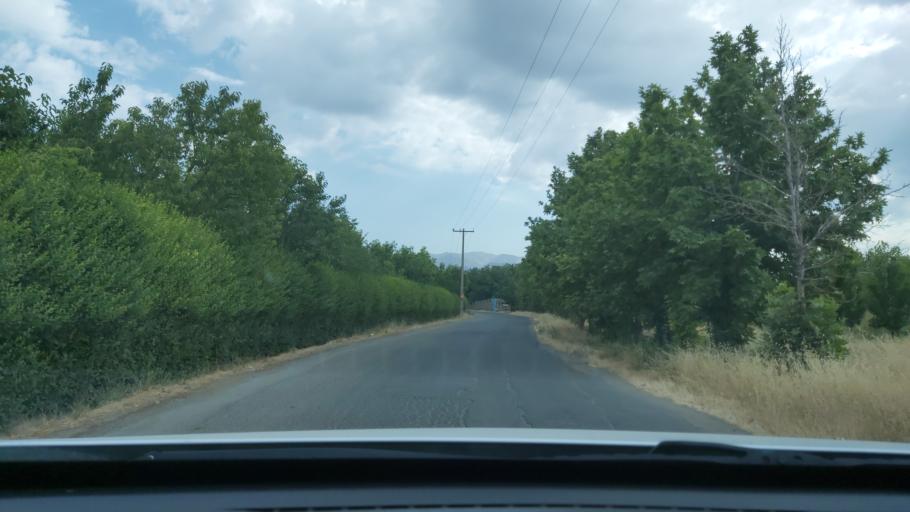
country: IR
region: Alborz
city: Hashtgerd
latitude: 35.9488
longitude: 50.7733
